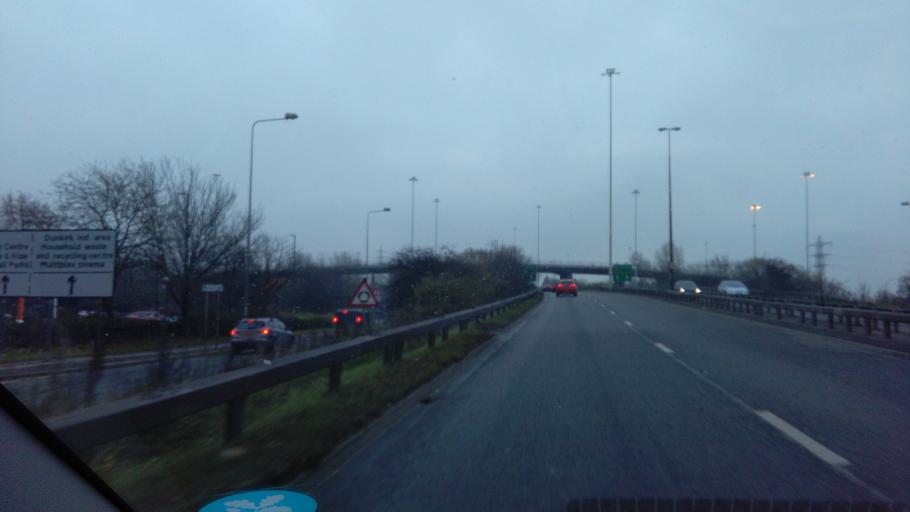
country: GB
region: England
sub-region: Nottingham
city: Nottingham
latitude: 52.9307
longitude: -1.1701
